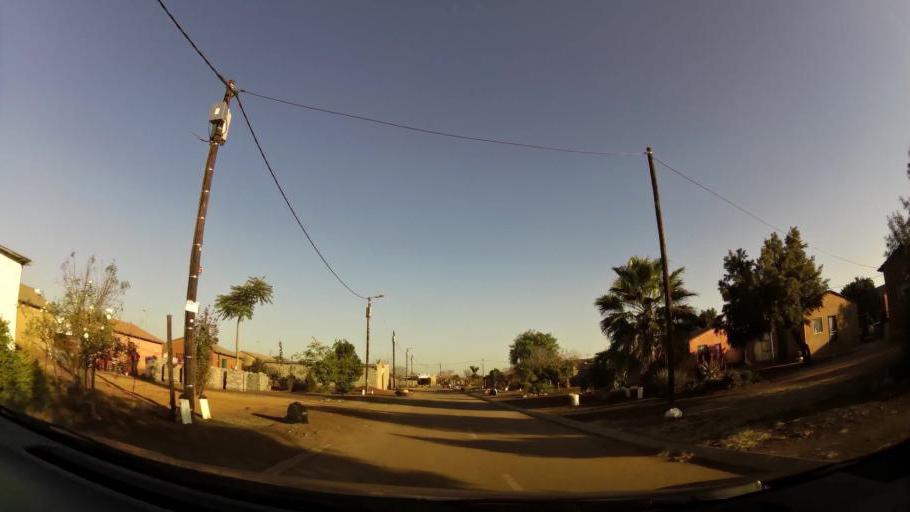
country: ZA
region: Gauteng
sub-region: City of Tshwane Metropolitan Municipality
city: Mabopane
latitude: -25.5995
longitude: 28.1038
